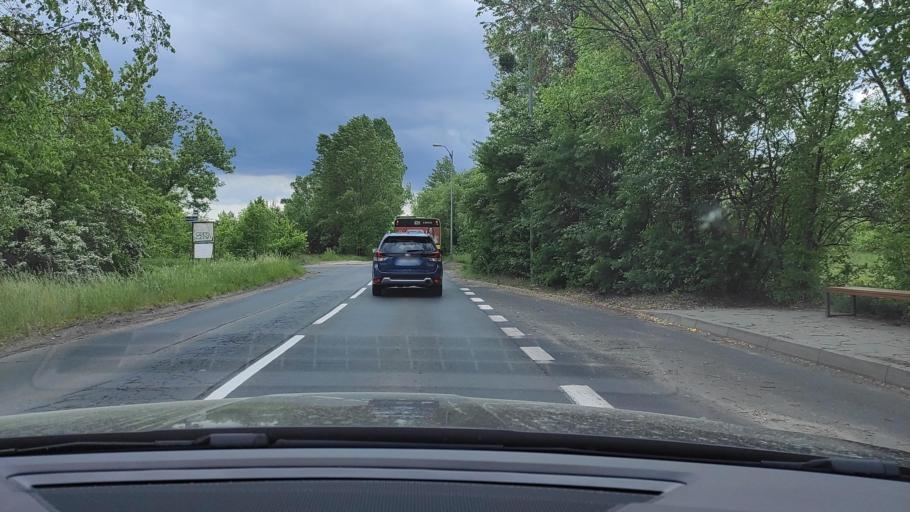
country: PL
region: Greater Poland Voivodeship
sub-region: Powiat poznanski
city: Swarzedz
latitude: 52.3882
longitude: 17.0292
